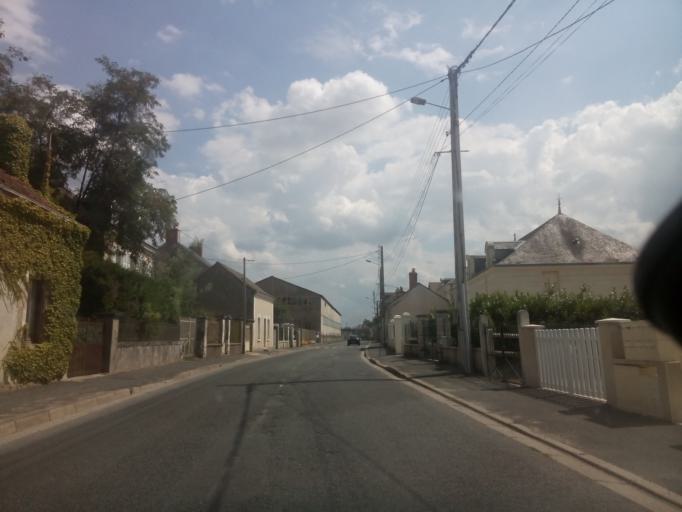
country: FR
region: Centre
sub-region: Departement d'Indre-et-Loire
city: Azay-le-Rideau
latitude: 47.2640
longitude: 0.4532
